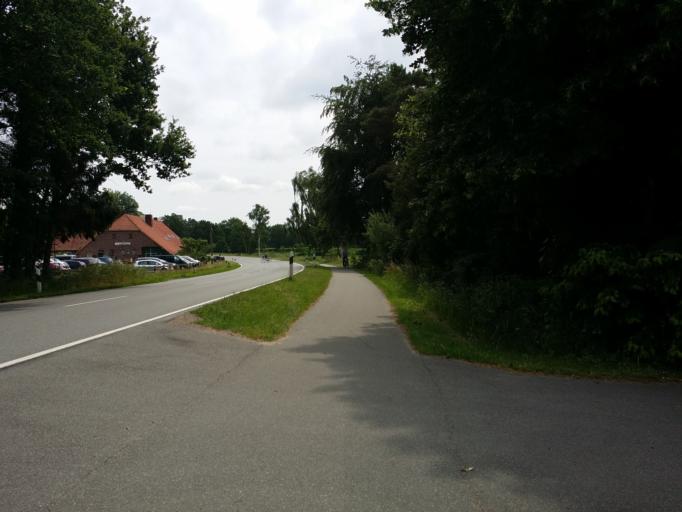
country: DE
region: Lower Saxony
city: Zetel
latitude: 53.3921
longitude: 7.9301
